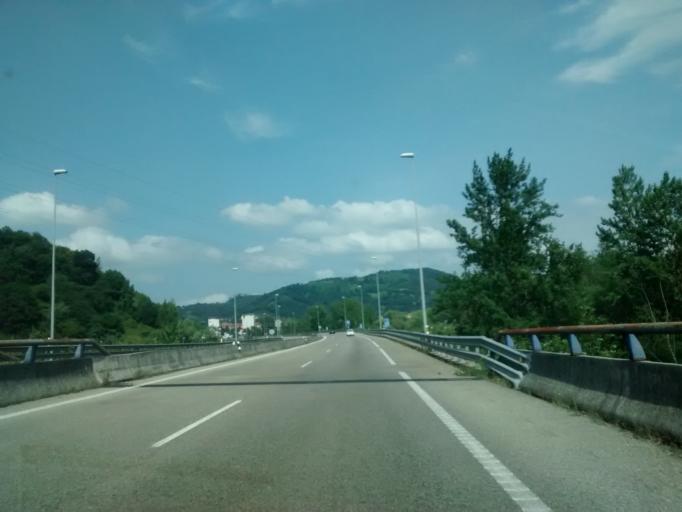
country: ES
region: Asturias
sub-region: Province of Asturias
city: Sama
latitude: 43.3223
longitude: -5.7392
